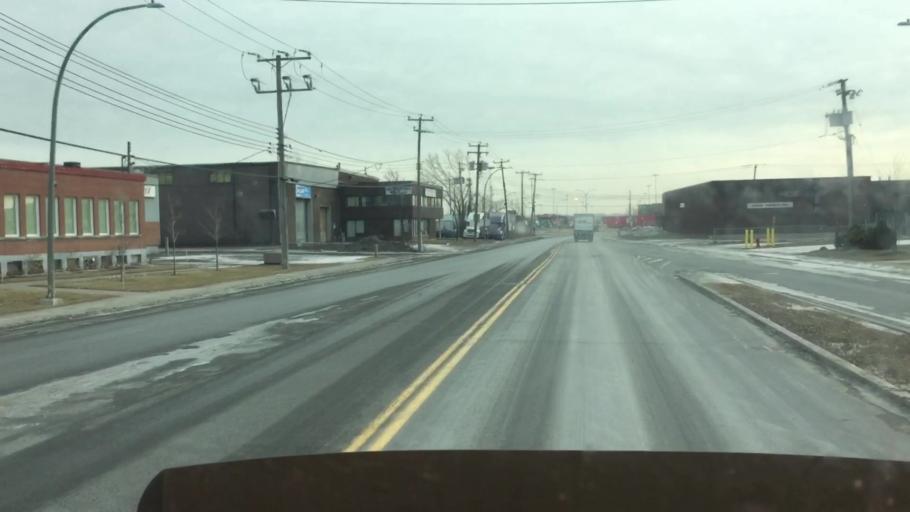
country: CA
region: Quebec
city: Dorval
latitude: 45.4634
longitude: -73.7173
